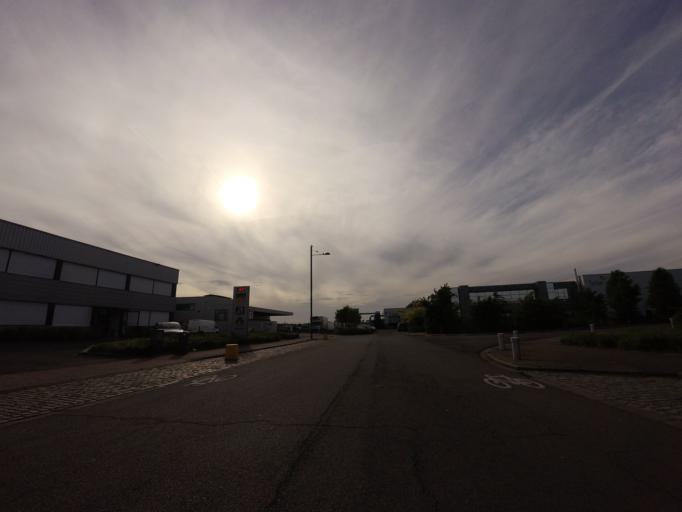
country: BE
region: Flanders
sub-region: Provincie Vlaams-Brabant
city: Diegem
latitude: 50.8855
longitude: 4.4195
